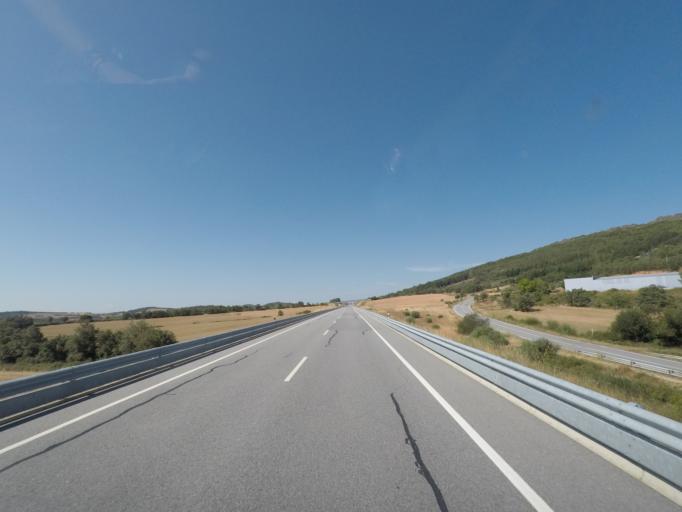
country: PT
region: Braganca
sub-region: Mogadouro
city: Mogadouro
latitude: 41.3484
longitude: -6.6109
